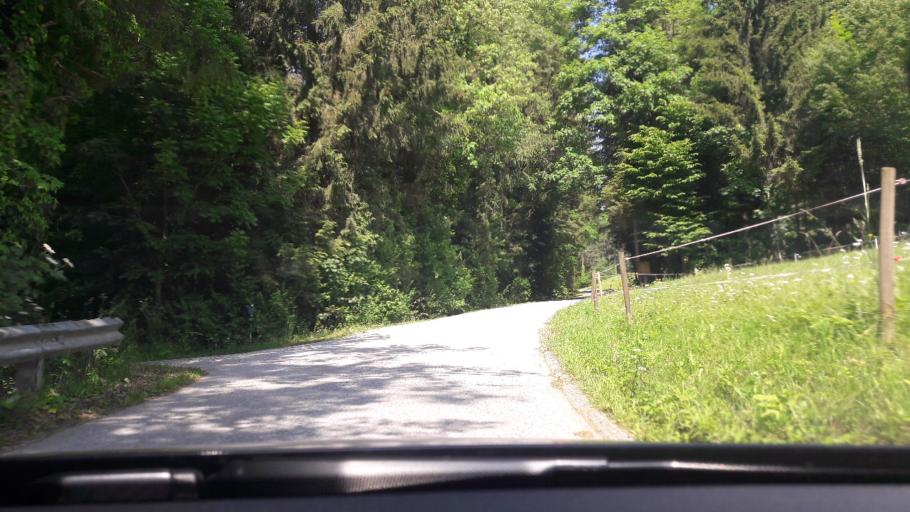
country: AT
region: Styria
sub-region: Politischer Bezirk Graz-Umgebung
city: Stiwoll
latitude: 47.1031
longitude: 15.2128
